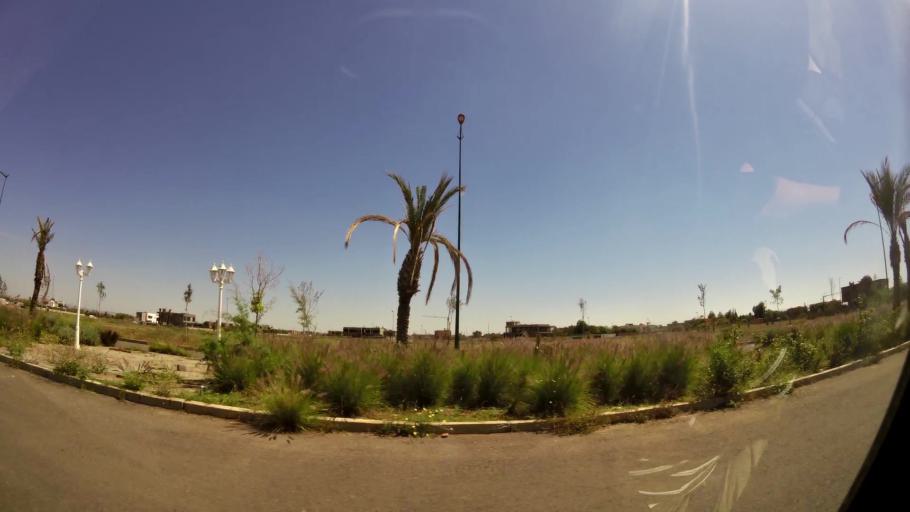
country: MA
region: Marrakech-Tensift-Al Haouz
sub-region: Marrakech
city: Marrakesh
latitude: 31.5913
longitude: -8.0025
